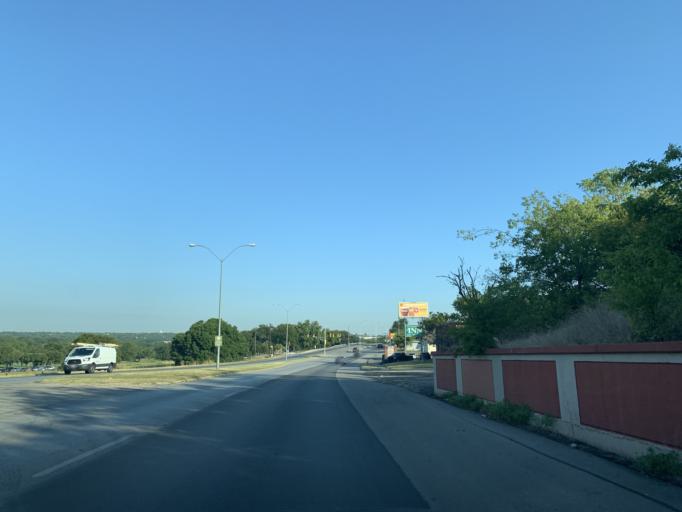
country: US
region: Texas
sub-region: Tarrant County
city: River Oaks
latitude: 32.7744
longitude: -97.3660
